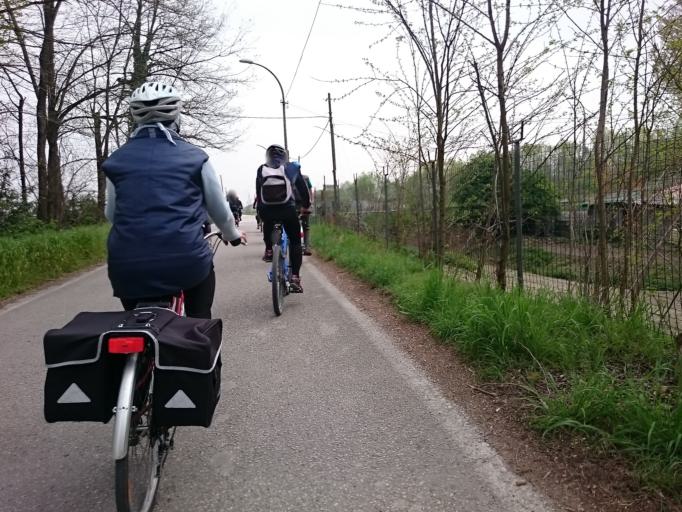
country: IT
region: Veneto
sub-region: Provincia di Padova
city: Anguillara Veneta
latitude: 45.1485
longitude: 11.8628
